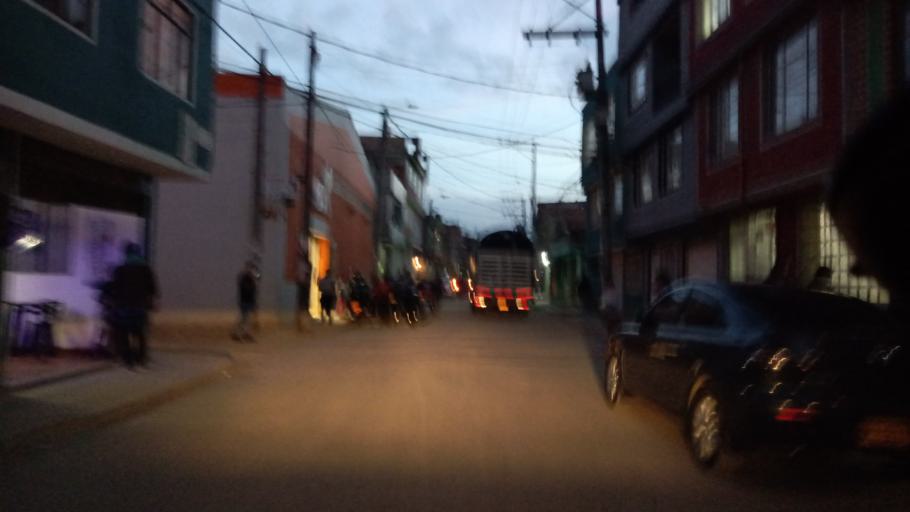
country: CO
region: Cundinamarca
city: Soacha
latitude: 4.5724
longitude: -74.2328
